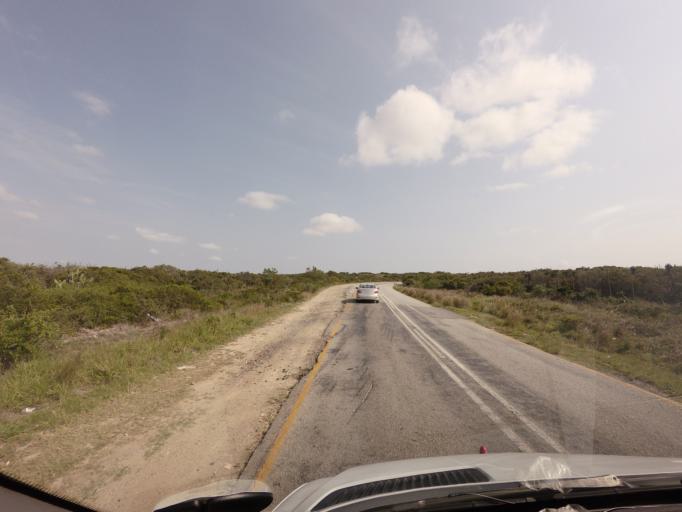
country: ZA
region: Eastern Cape
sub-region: Nelson Mandela Bay Metropolitan Municipality
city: Uitenhage
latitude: -33.7083
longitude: 25.5880
